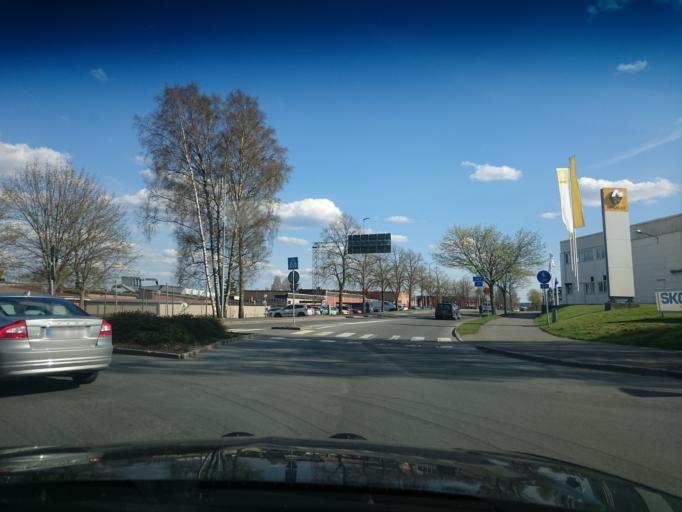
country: SE
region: Joenkoeping
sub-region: Vetlanda Kommun
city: Vetlanda
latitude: 57.4212
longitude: 15.0805
